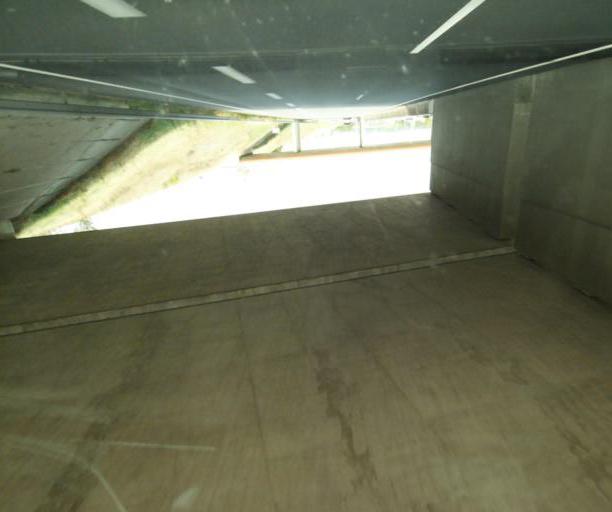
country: FR
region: Lower Normandy
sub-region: Departement de l'Orne
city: Valframbert
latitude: 48.4543
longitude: 0.1307
